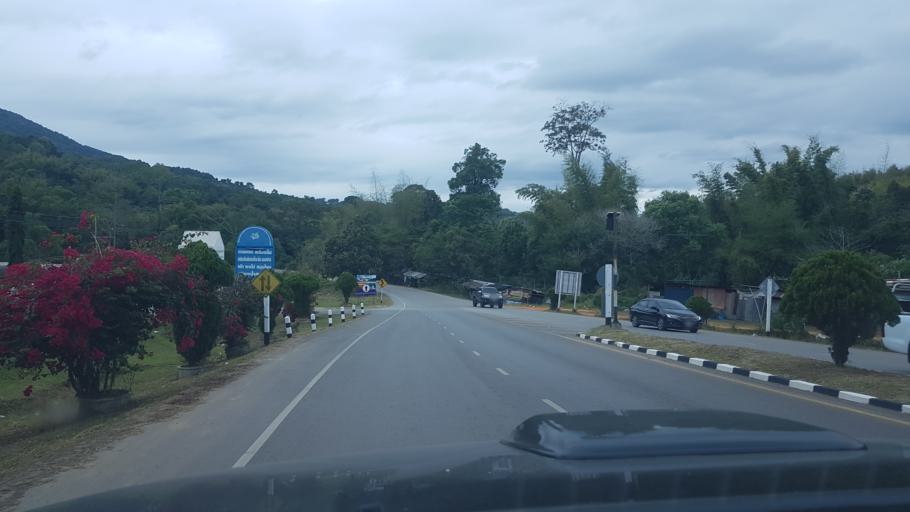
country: TH
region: Phetchabun
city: Khao Kho
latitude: 16.5711
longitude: 100.9878
